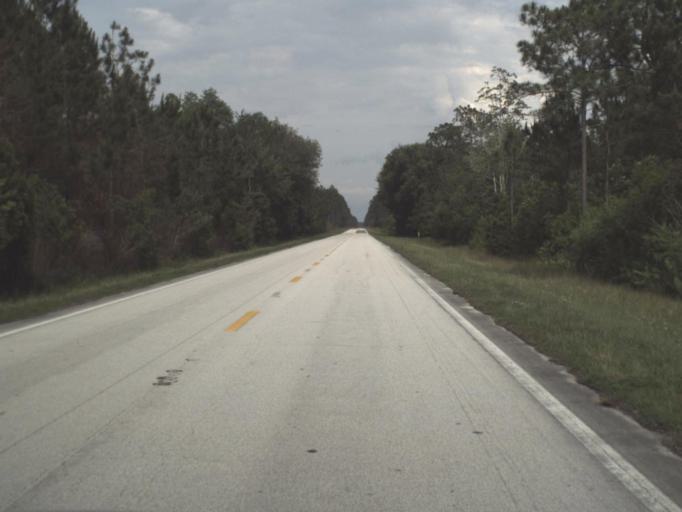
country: US
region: Florida
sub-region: Columbia County
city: Five Points
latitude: 30.5683
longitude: -82.4343
